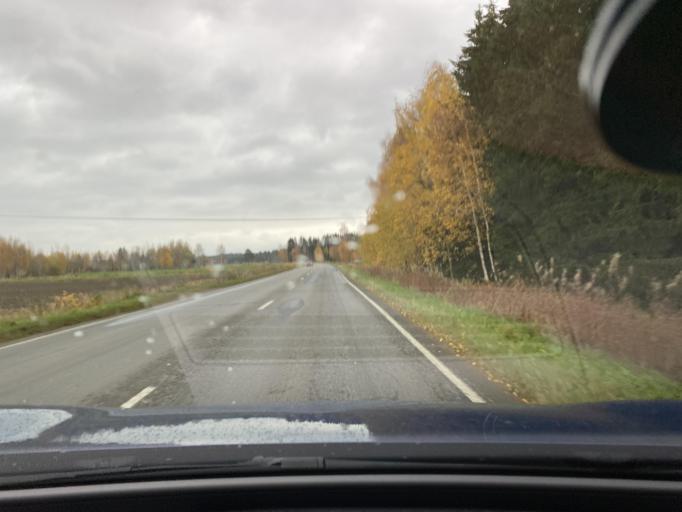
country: FI
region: Satakunta
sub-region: Rauma
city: Saekylae
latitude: 61.0397
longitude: 22.3962
